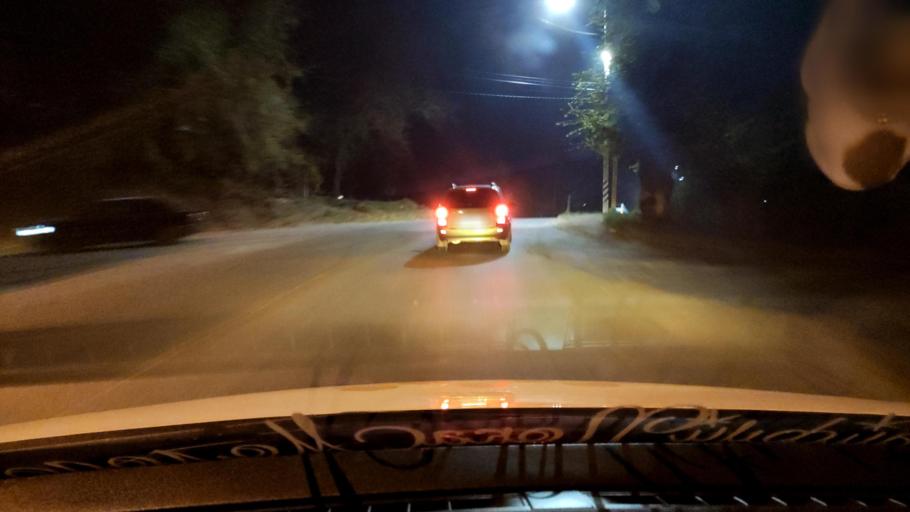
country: RU
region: Voronezj
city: Semiluki
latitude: 51.6771
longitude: 39.0303
